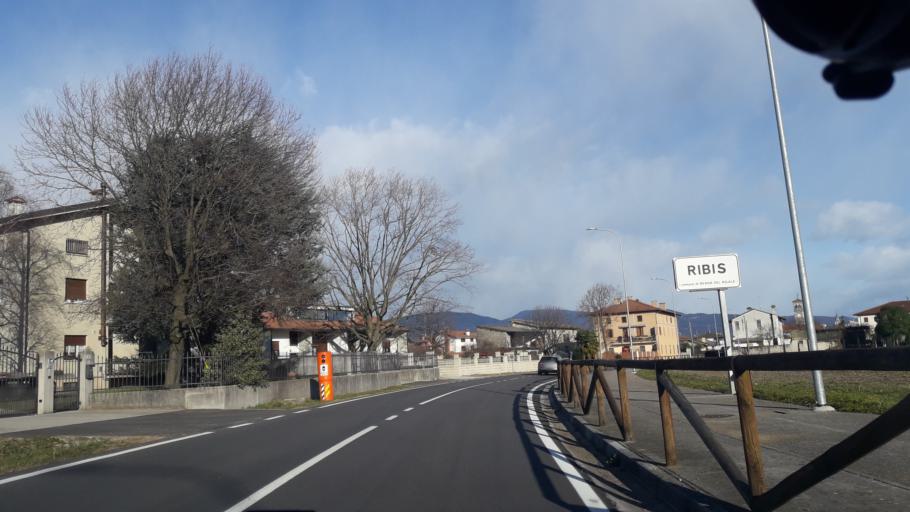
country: IT
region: Friuli Venezia Giulia
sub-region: Provincia di Udine
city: Reana del Rojale
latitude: 46.1363
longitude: 13.2371
